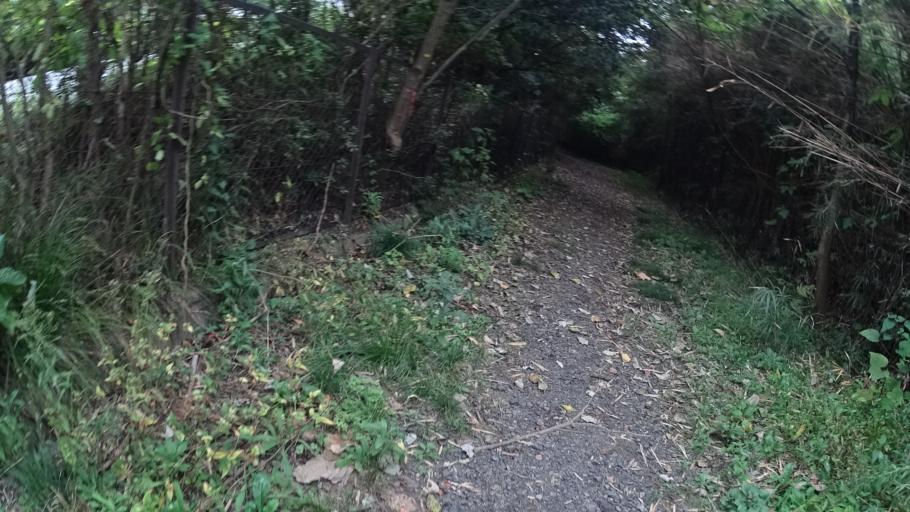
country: JP
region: Kanagawa
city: Kamakura
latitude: 35.3525
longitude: 139.5946
